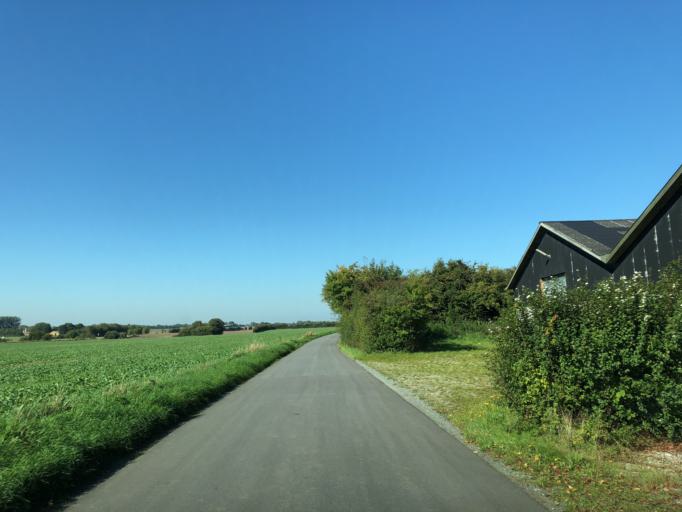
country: DK
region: South Denmark
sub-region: Sonderborg Kommune
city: Dybbol
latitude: 54.9336
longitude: 9.7329
